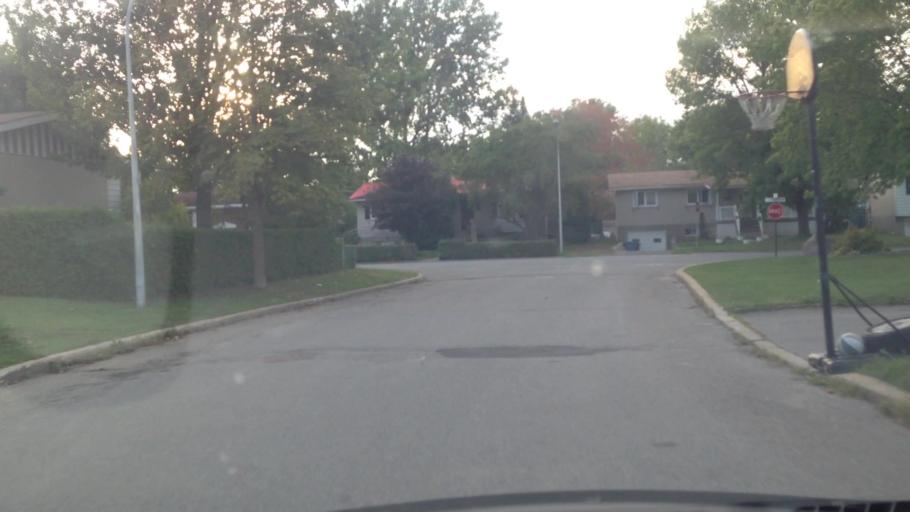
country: CA
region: Quebec
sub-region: Monteregie
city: Mercier
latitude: 45.3461
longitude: -73.7164
